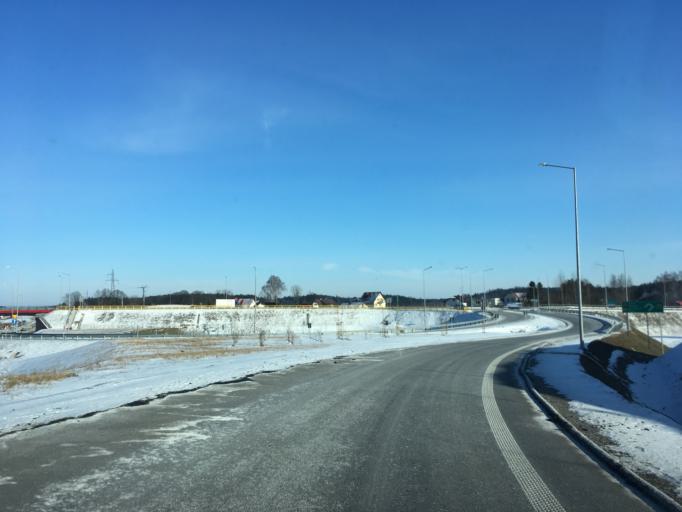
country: PL
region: Pomeranian Voivodeship
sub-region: Powiat koscierski
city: Koscierzyna
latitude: 54.1076
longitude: 17.9732
